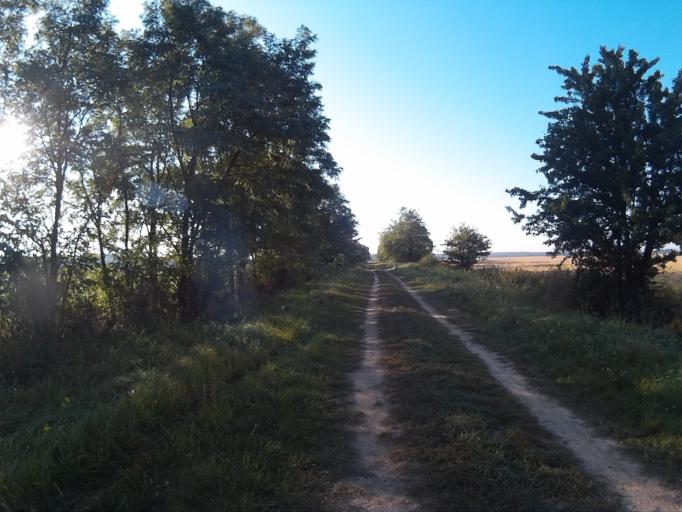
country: HU
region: Vas
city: Jak
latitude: 47.1243
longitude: 16.5890
